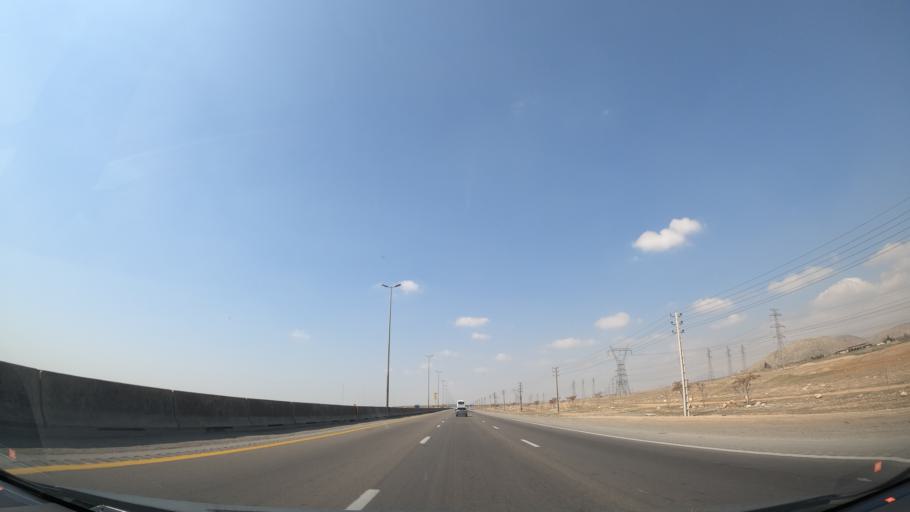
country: IR
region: Qazvin
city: Abyek
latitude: 36.0611
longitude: 50.4967
